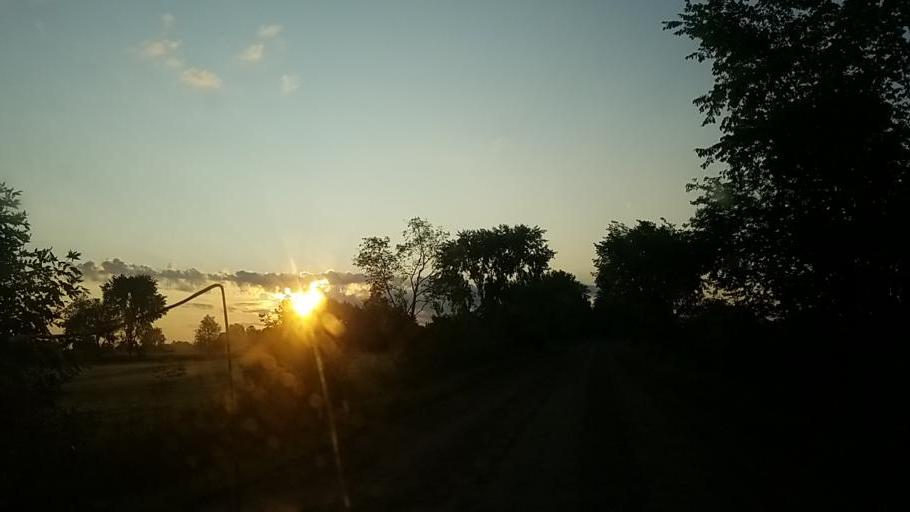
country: US
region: Michigan
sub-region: Osceola County
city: Evart
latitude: 43.9152
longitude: -85.1947
